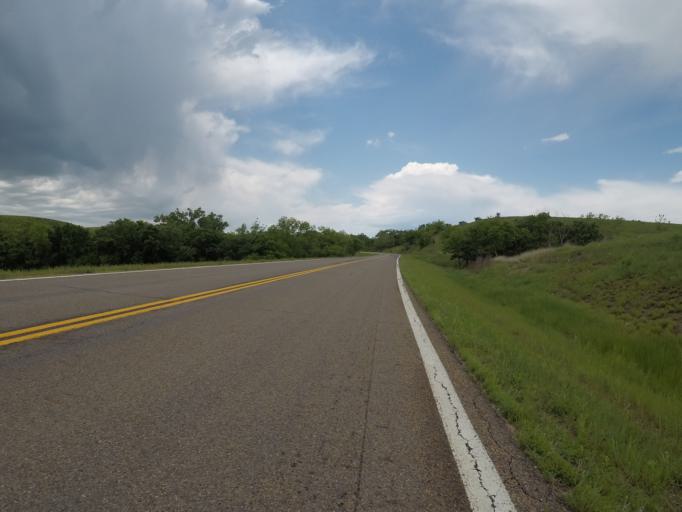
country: US
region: Kansas
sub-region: Wabaunsee County
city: Alma
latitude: 38.8672
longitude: -96.2971
